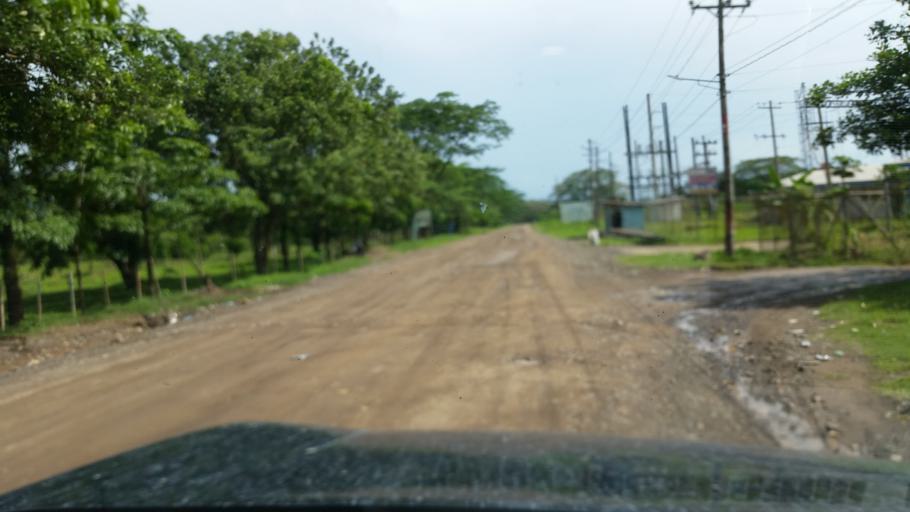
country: NI
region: Atlantico Norte (RAAN)
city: Siuna
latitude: 13.7109
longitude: -84.7756
